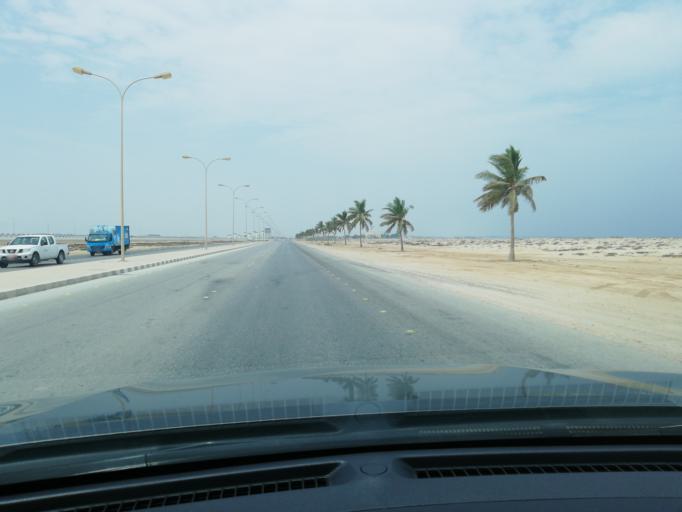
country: OM
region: Zufar
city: Salalah
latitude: 16.9725
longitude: 54.0034
